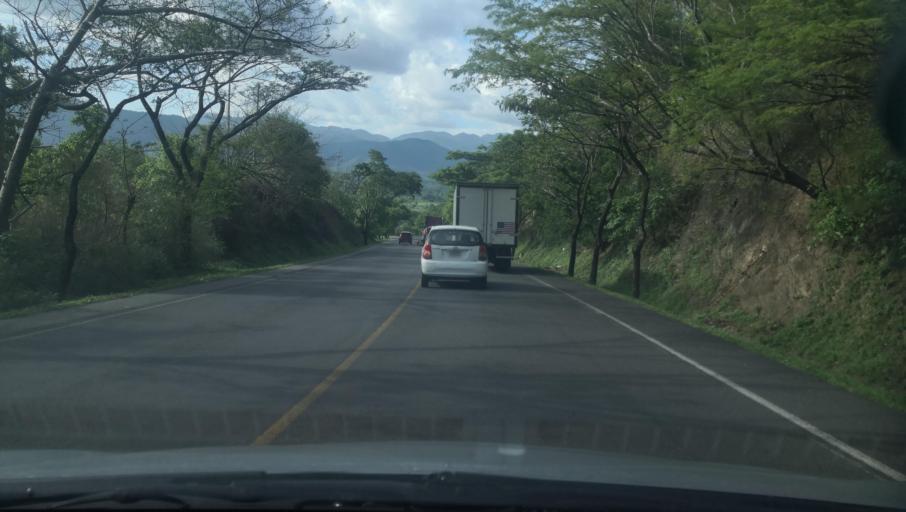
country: NI
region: Nueva Segovia
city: Ocotal
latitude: 13.6008
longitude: -86.4722
